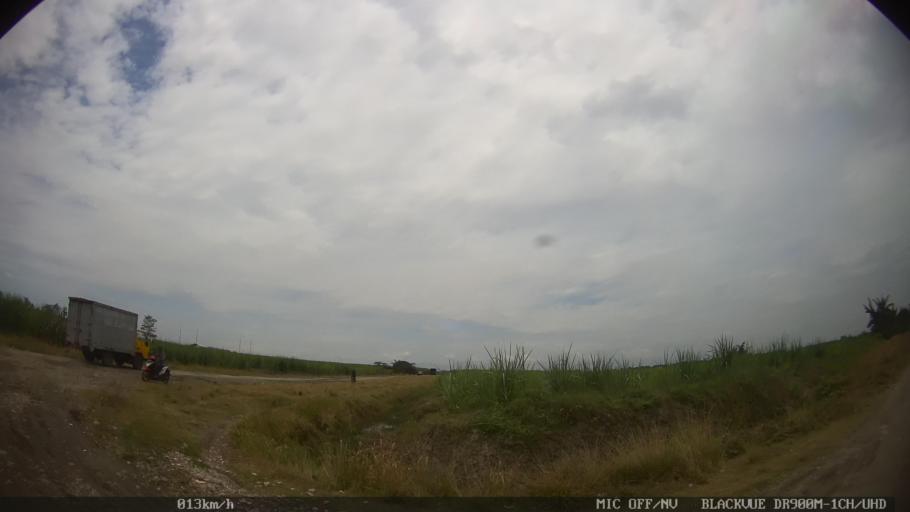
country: ID
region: North Sumatra
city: Sunggal
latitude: 3.6366
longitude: 98.5773
